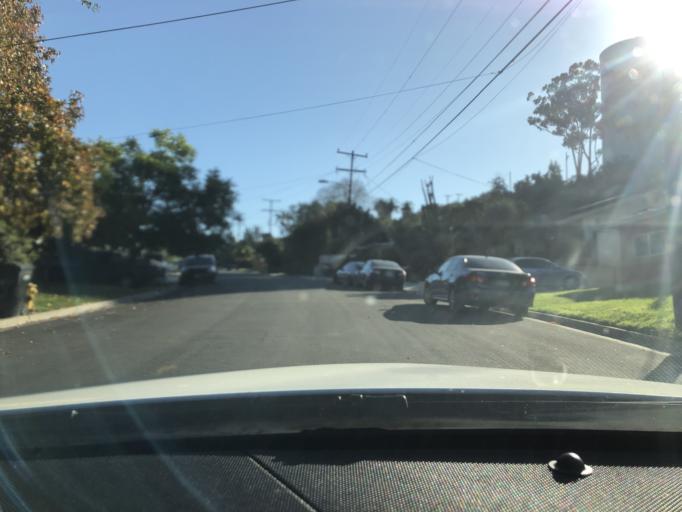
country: US
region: California
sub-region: San Diego County
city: Lemon Grove
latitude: 32.7500
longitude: -117.0662
